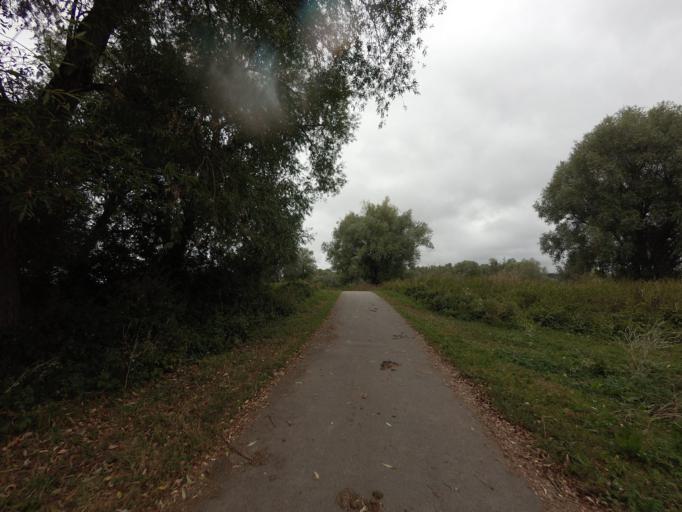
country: NL
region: Gelderland
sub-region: Gemeente Arnhem
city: Sterrenberg
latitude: 51.9723
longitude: 5.8803
